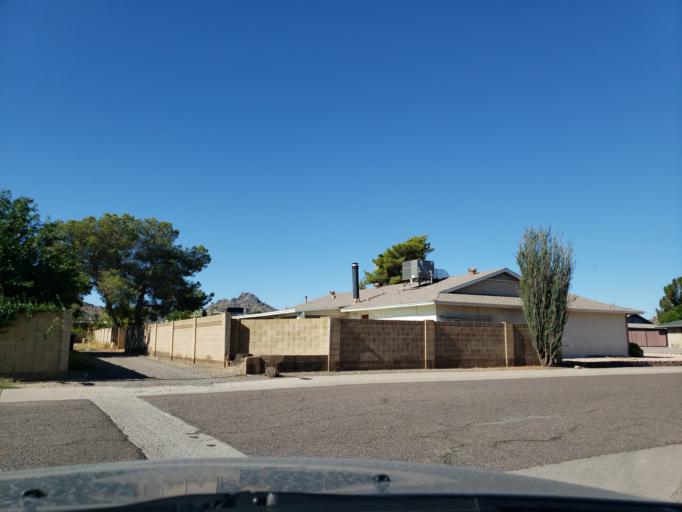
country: US
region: Arizona
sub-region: Maricopa County
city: Paradise Valley
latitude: 33.5813
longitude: -112.0078
